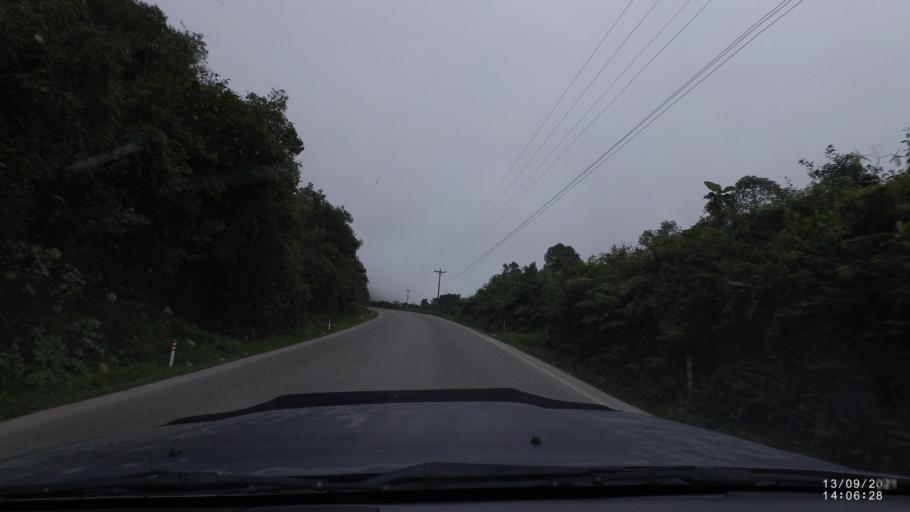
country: BO
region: Cochabamba
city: Colomi
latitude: -17.1878
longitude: -65.8831
